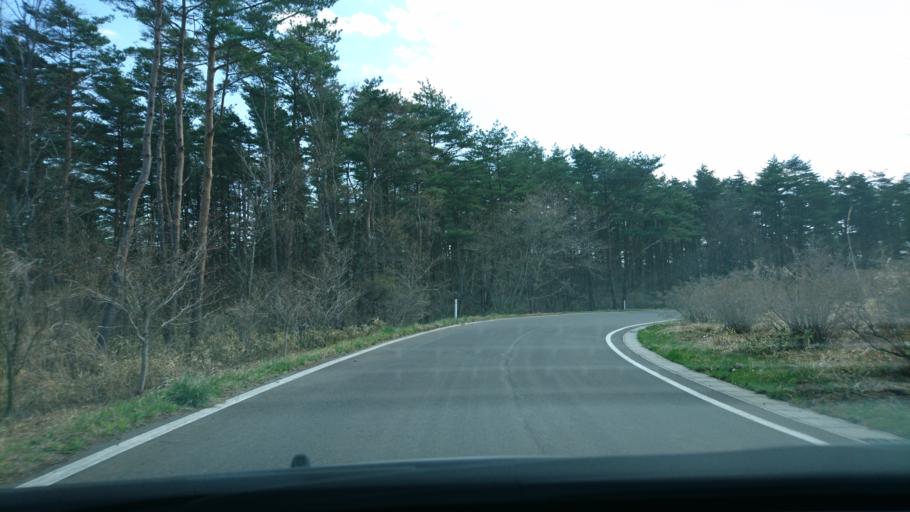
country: JP
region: Iwate
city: Ofunato
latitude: 38.9648
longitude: 141.4525
